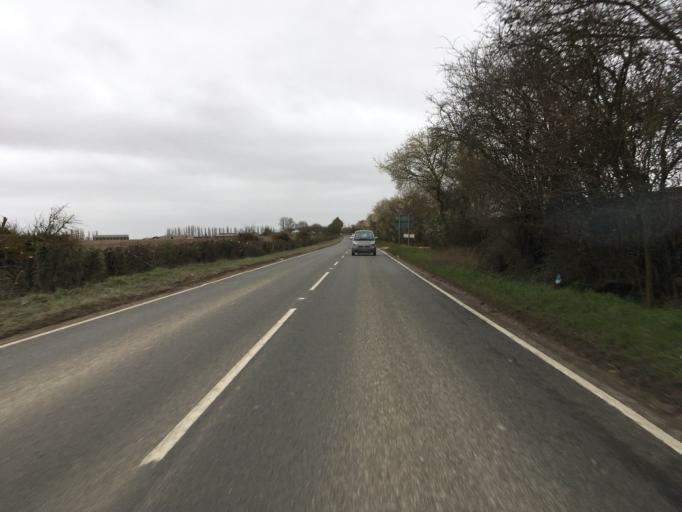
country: GB
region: England
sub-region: Oxfordshire
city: Stanford in the Vale
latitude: 51.6185
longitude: -1.4948
